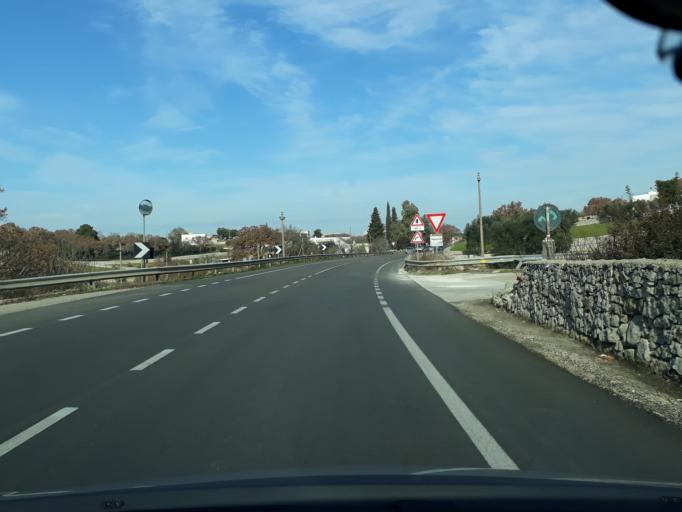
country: IT
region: Apulia
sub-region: Provincia di Bari
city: Locorotondo
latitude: 40.7833
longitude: 17.3394
